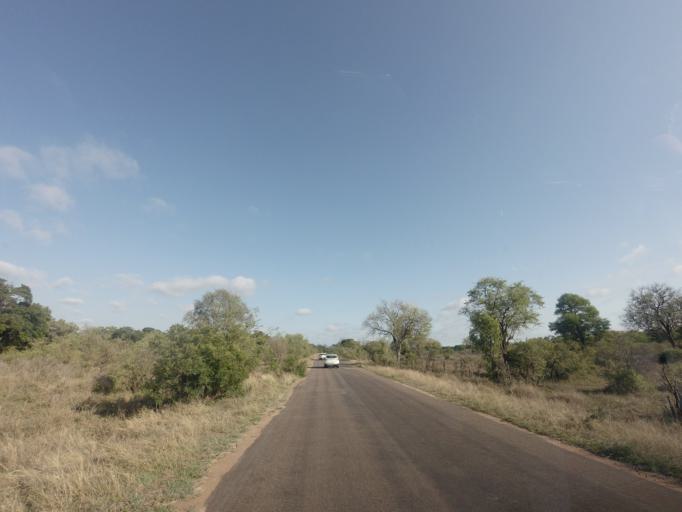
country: ZA
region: Mpumalanga
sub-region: Ehlanzeni District
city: Komatipoort
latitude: -25.2774
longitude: 31.8498
